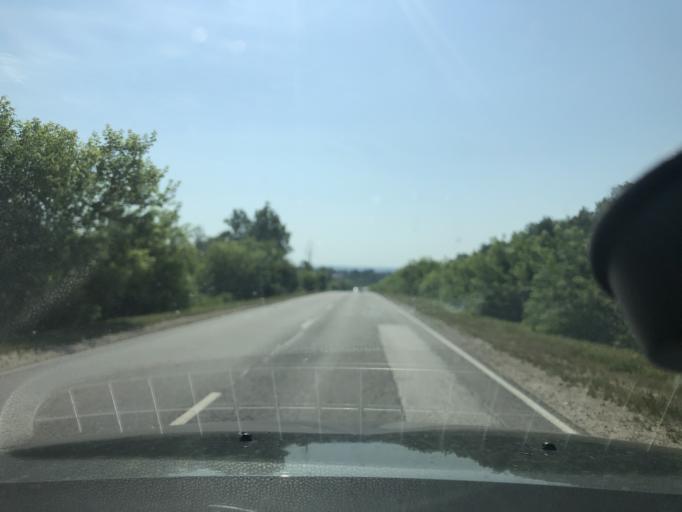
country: RU
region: Tula
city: Dubna
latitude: 54.1118
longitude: 37.0961
